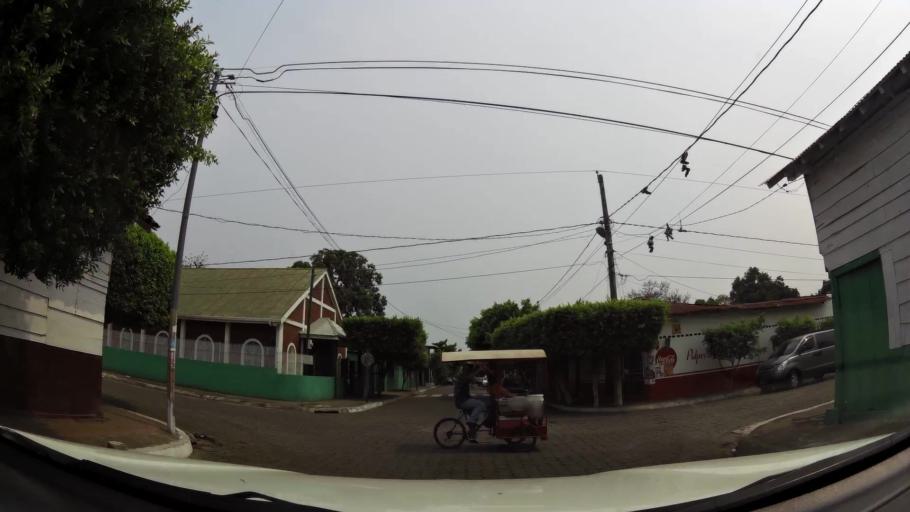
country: NI
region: Chinandega
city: Chinandega
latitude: 12.6252
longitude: -87.1364
